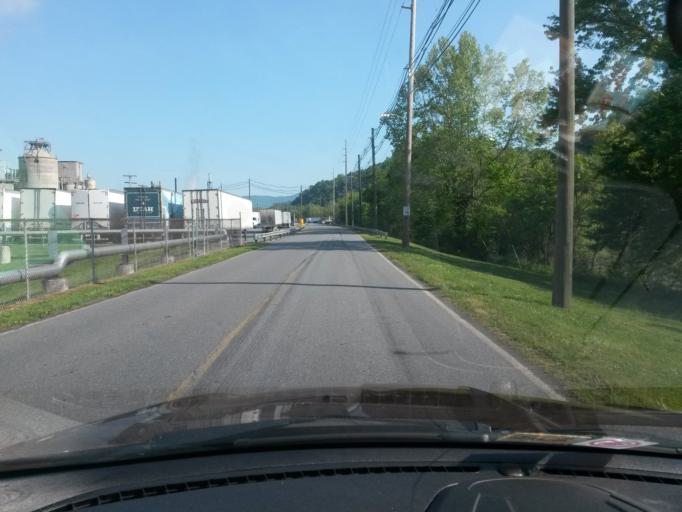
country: US
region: Virginia
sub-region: Rockbridge County
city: Glasgow
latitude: 37.5280
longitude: -79.3524
